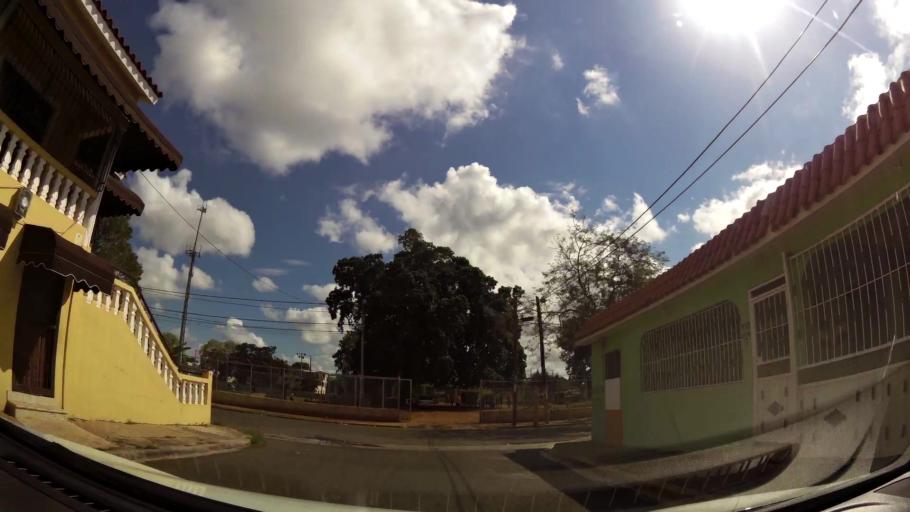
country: DO
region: Santo Domingo
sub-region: Santo Domingo
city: Santo Domingo Este
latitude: 18.5075
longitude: -69.8474
